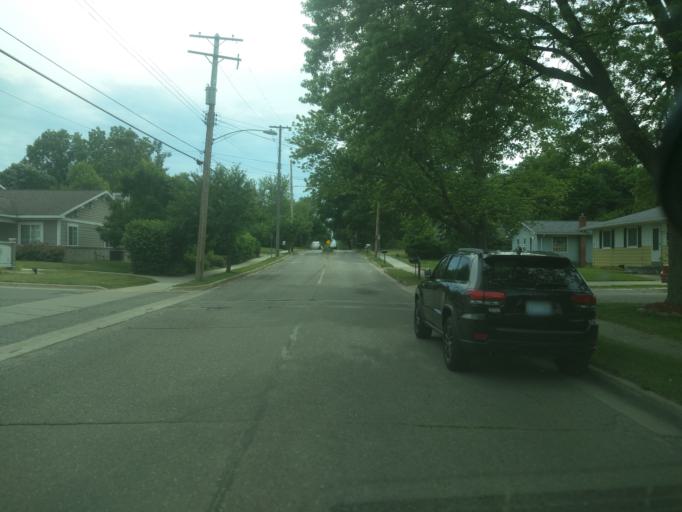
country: US
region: Michigan
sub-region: Ingham County
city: Lansing
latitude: 42.6911
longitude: -84.5700
